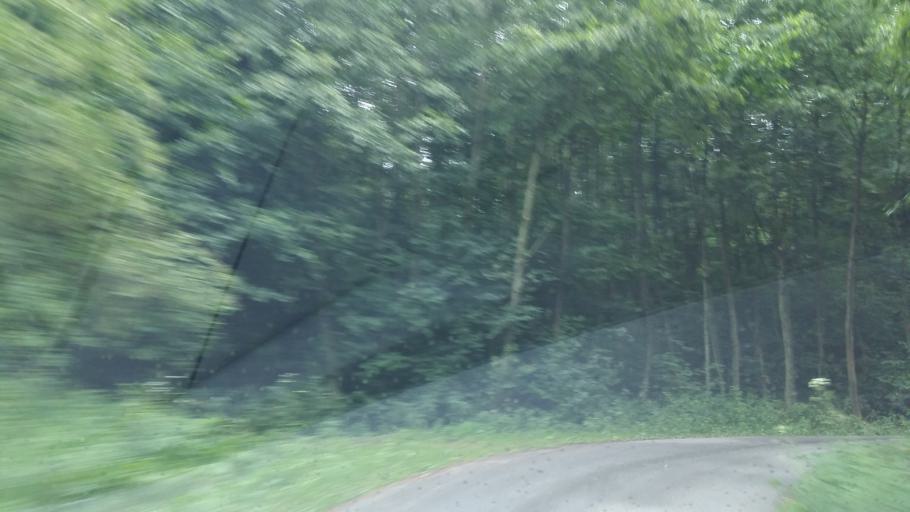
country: PL
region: Lesser Poland Voivodeship
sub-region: Powiat wadowicki
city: Spytkowice
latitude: 49.9813
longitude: 19.5064
